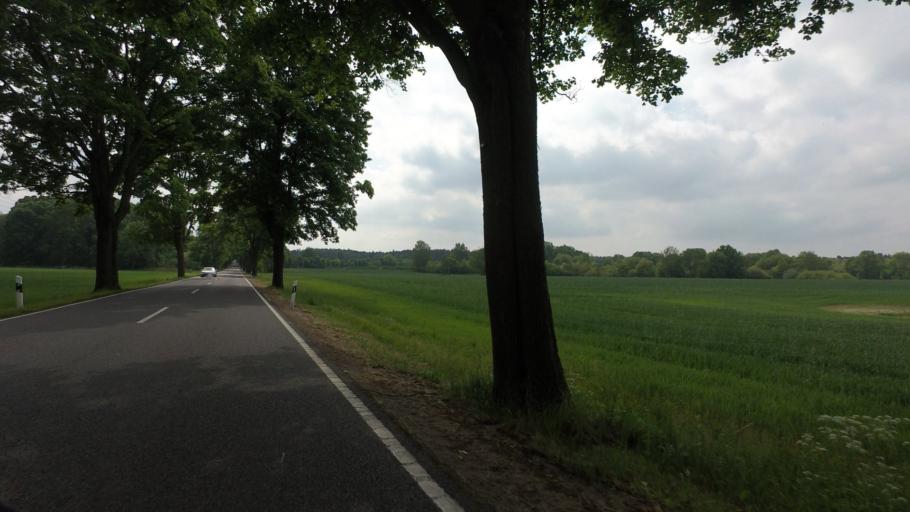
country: DE
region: Brandenburg
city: Lieberose
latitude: 51.9696
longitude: 14.3101
